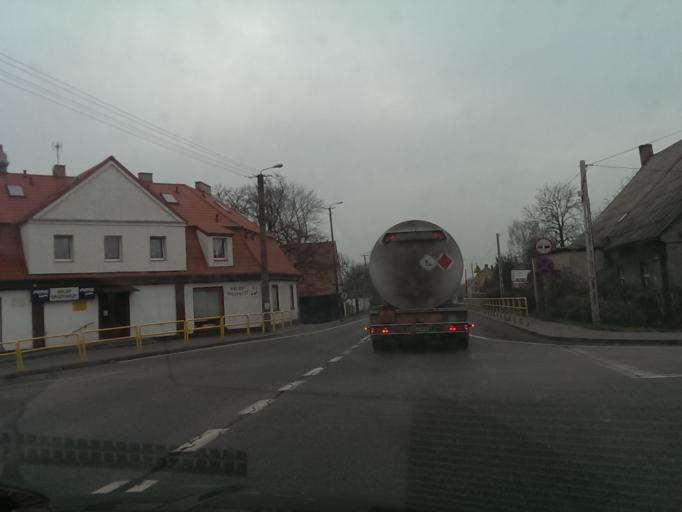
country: PL
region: Kujawsko-Pomorskie
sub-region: Powiat nakielski
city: Slesin
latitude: 53.1649
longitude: 17.7036
